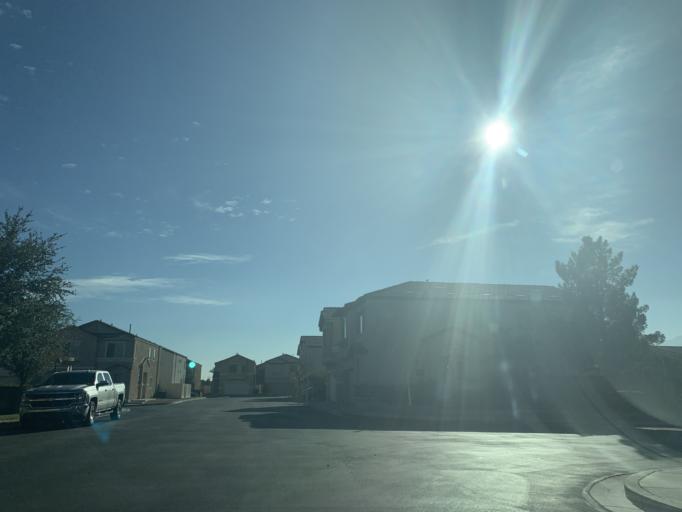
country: US
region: Nevada
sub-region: Clark County
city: Summerlin South
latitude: 36.3130
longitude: -115.3055
